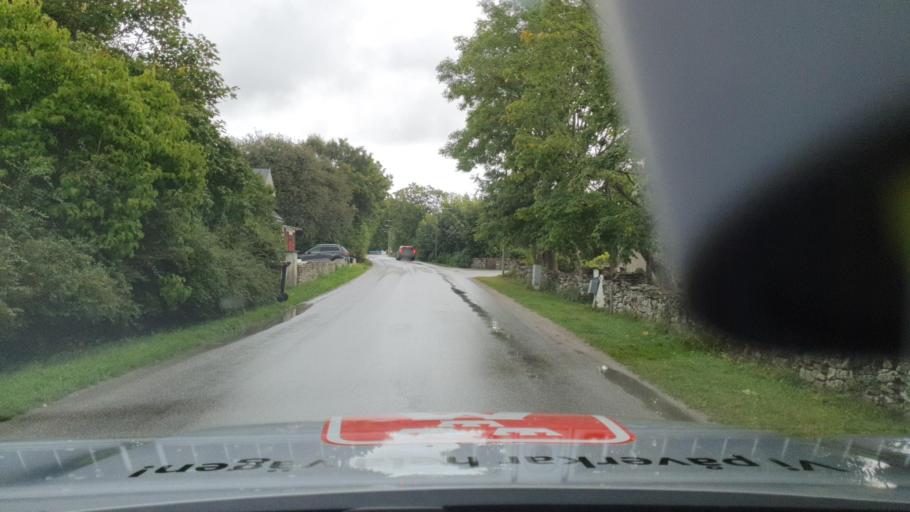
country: SE
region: Gotland
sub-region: Gotland
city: Hemse
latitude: 57.0308
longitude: 18.2715
